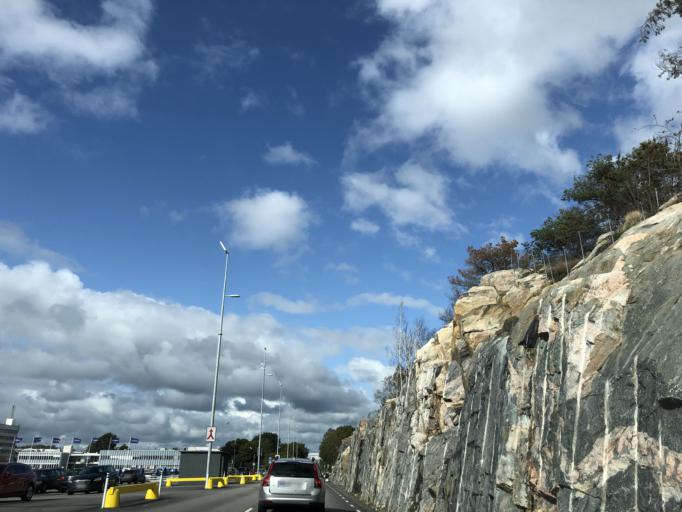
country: SE
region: Vaestra Goetaland
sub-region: Goteborg
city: Torslanda
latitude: 57.7166
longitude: 11.8432
